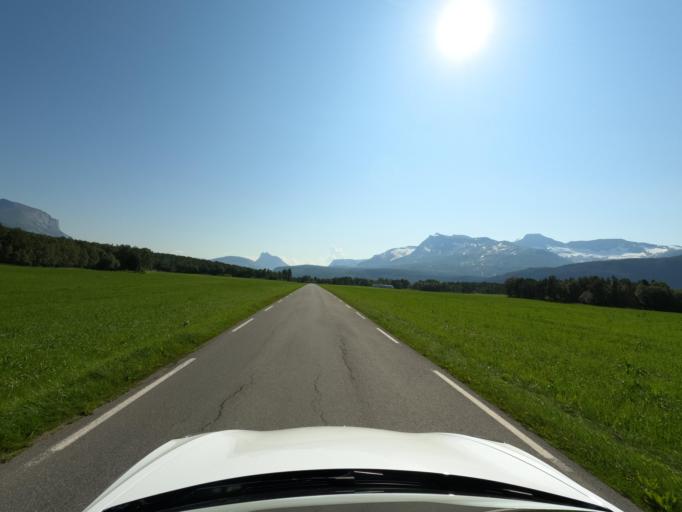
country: NO
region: Nordland
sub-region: Narvik
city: Narvik
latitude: 68.3238
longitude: 17.2888
